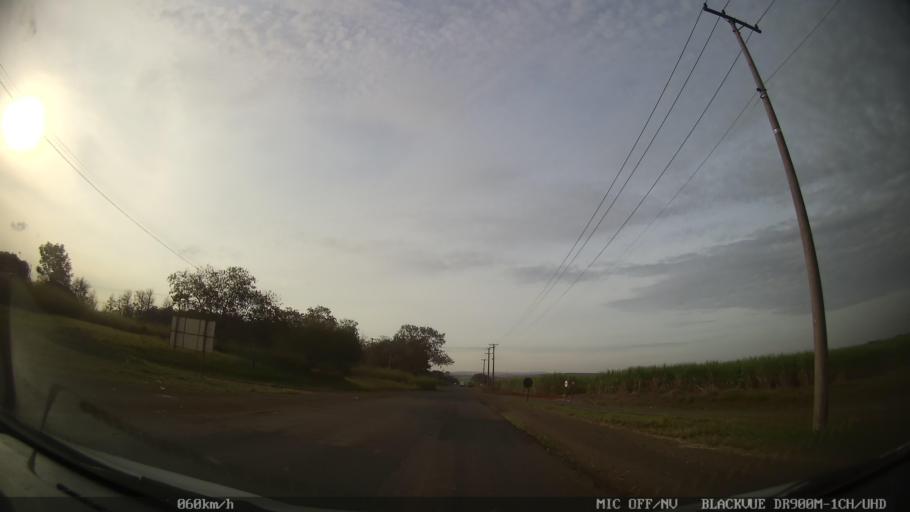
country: BR
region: Sao Paulo
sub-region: Piracicaba
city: Piracicaba
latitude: -22.7222
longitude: -47.5840
